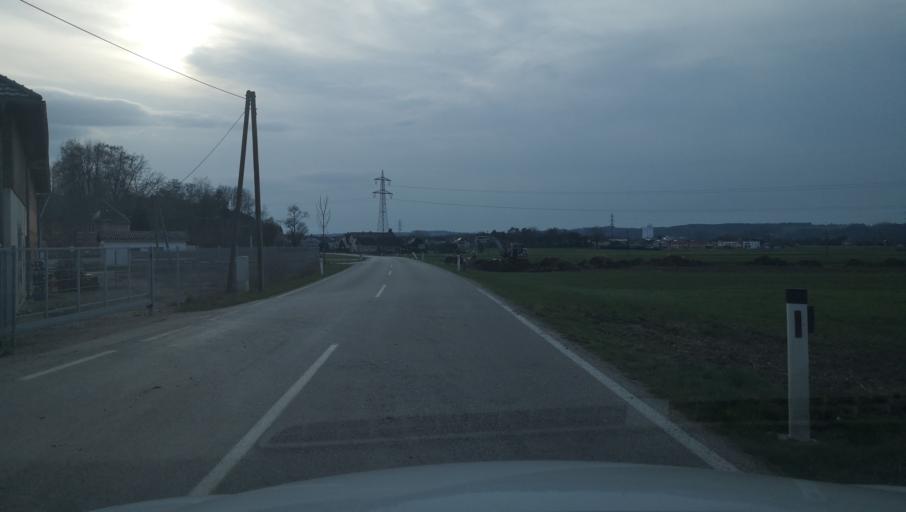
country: AT
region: Lower Austria
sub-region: Politischer Bezirk Amstetten
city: Amstetten
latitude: 48.0968
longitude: 14.8654
